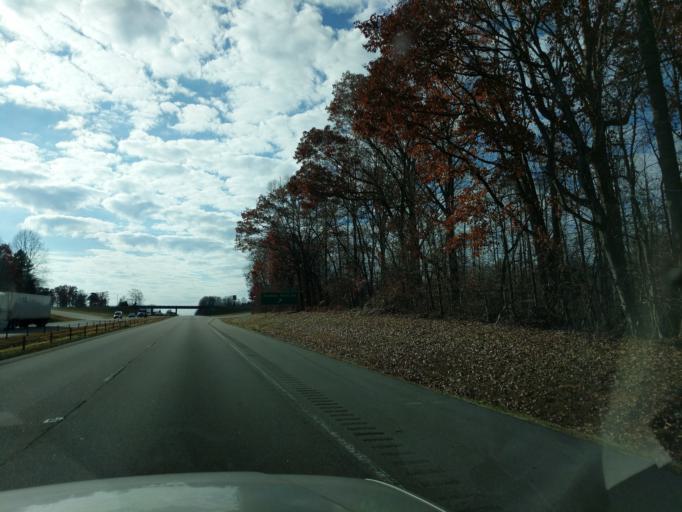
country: US
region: North Carolina
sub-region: Iredell County
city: Statesville
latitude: 35.7832
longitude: -80.9680
